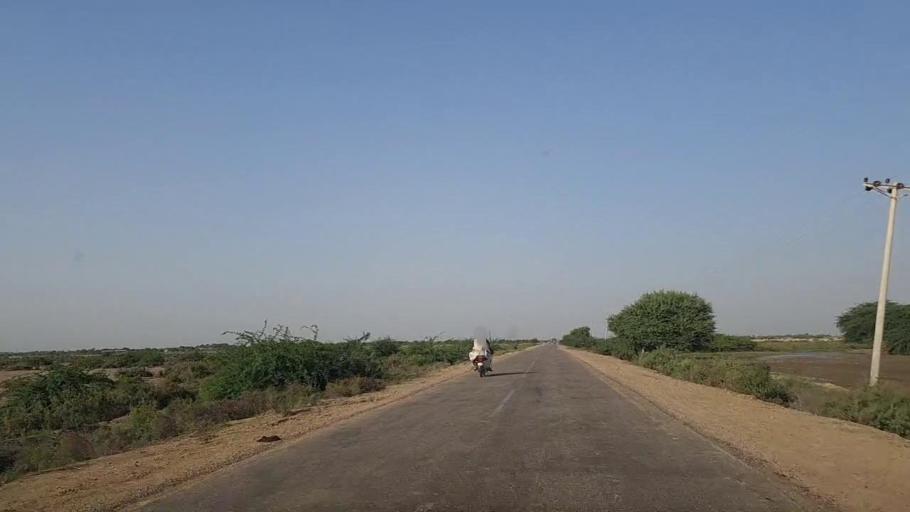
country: PK
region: Sindh
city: Mirpur Batoro
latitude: 24.6096
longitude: 68.4031
